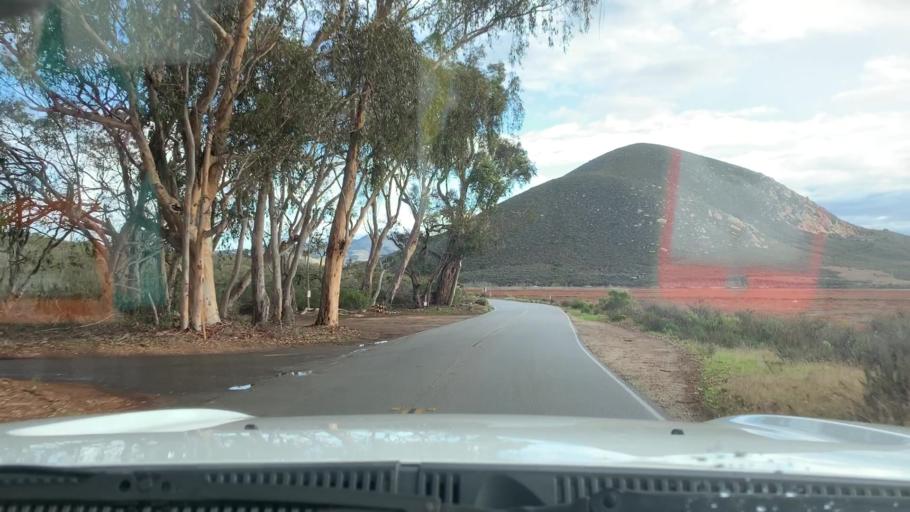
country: US
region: California
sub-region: San Luis Obispo County
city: Morro Bay
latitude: 35.3474
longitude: -120.8353
